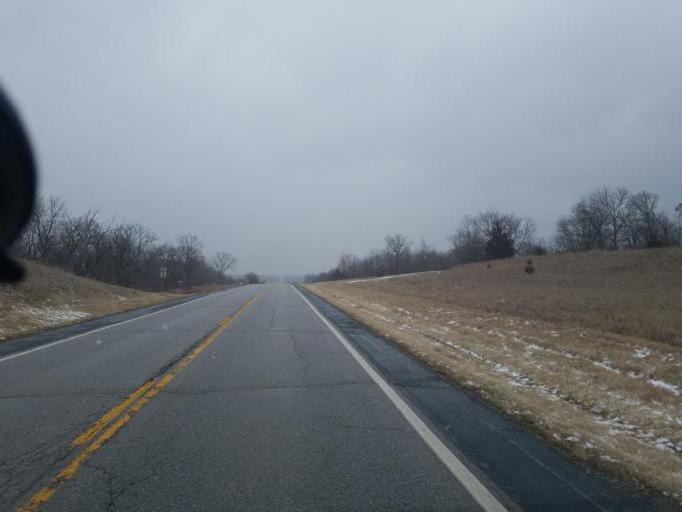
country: US
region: Missouri
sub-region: Putnam County
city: Unionville
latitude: 40.4654
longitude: -92.8948
